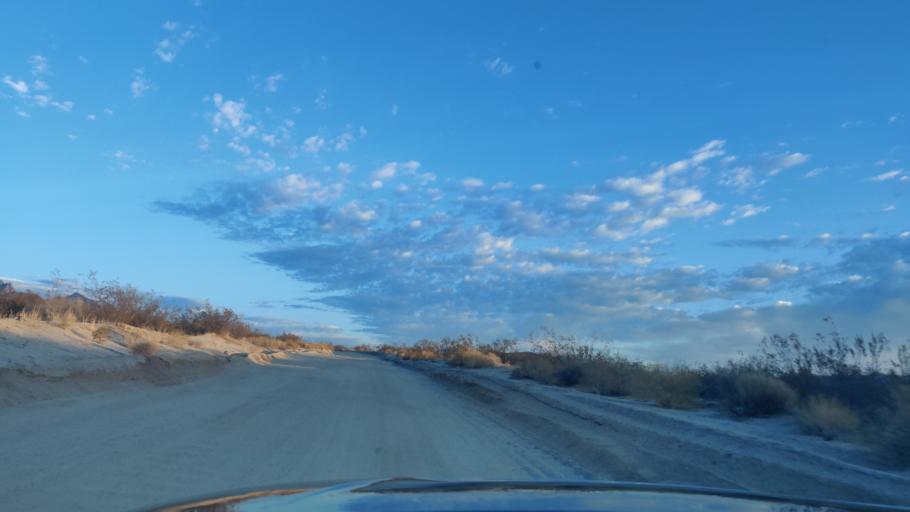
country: US
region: Nevada
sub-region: Clark County
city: Laughlin
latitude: 35.2145
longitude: -114.6749
